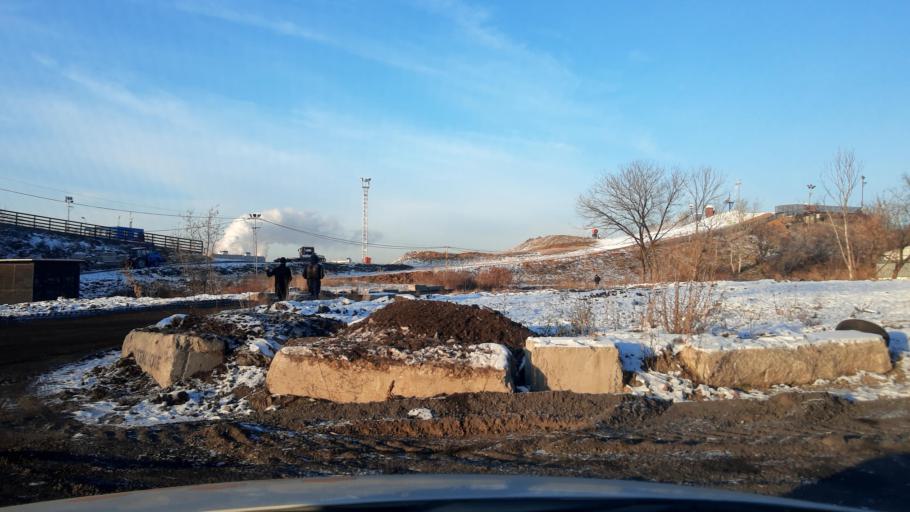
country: RU
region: Moscow
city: Kotlovka
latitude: 55.6782
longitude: 37.6167
